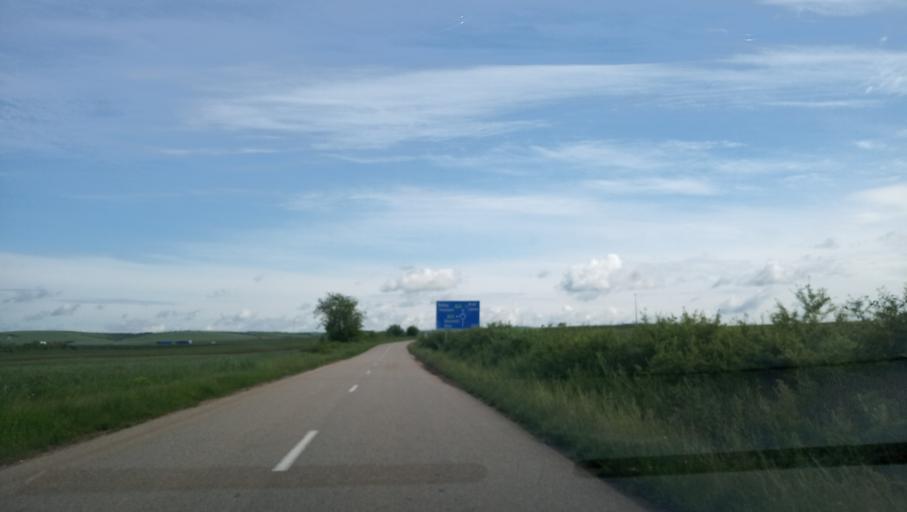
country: RO
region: Timis
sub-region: Comuna Topolovatu Mare
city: Topolovatu Mare
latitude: 45.7935
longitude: 21.6545
